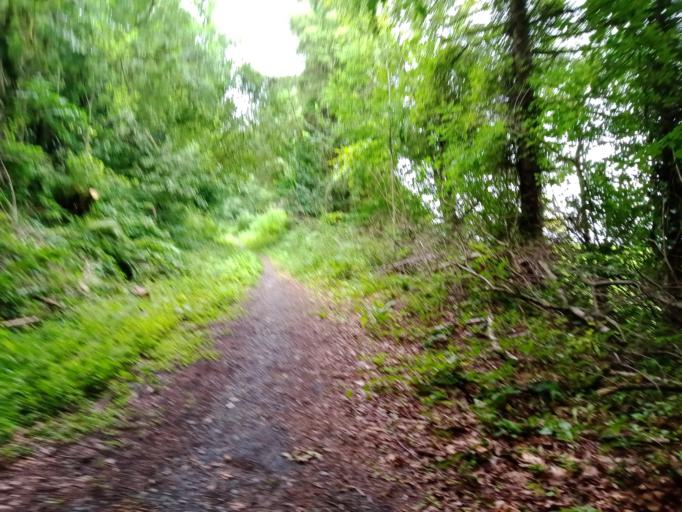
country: IE
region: Leinster
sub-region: Kilkenny
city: Ballyragget
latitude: 52.8283
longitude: -7.3980
